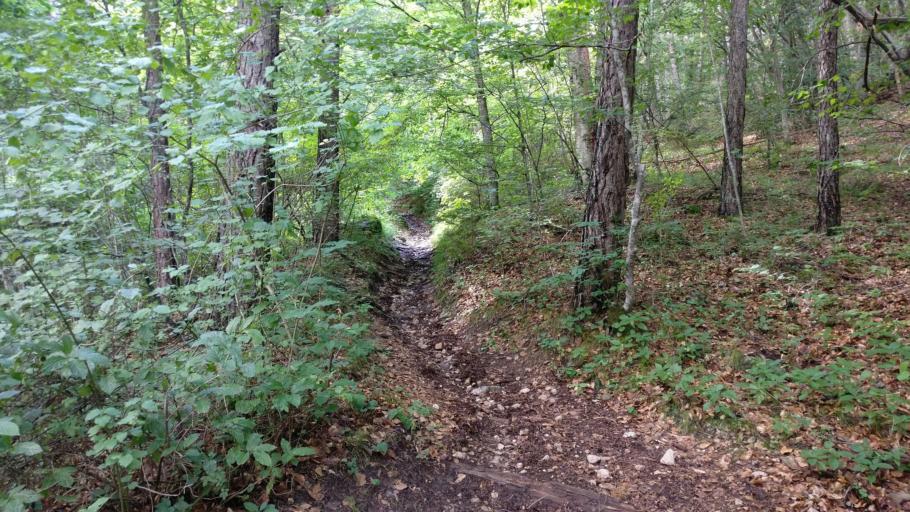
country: IT
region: Trentino-Alto Adige
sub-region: Bolzano
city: San Paolo
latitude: 46.4738
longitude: 11.2343
